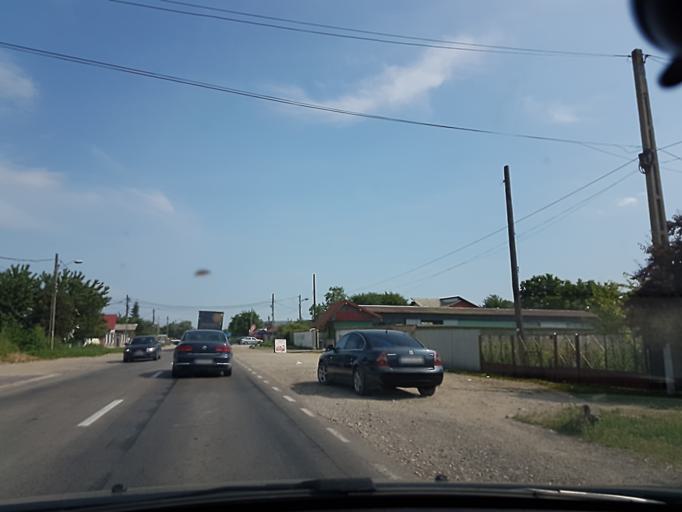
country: RO
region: Prahova
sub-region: Comuna Blejoiu
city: Blejoi
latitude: 45.0074
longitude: 26.0154
